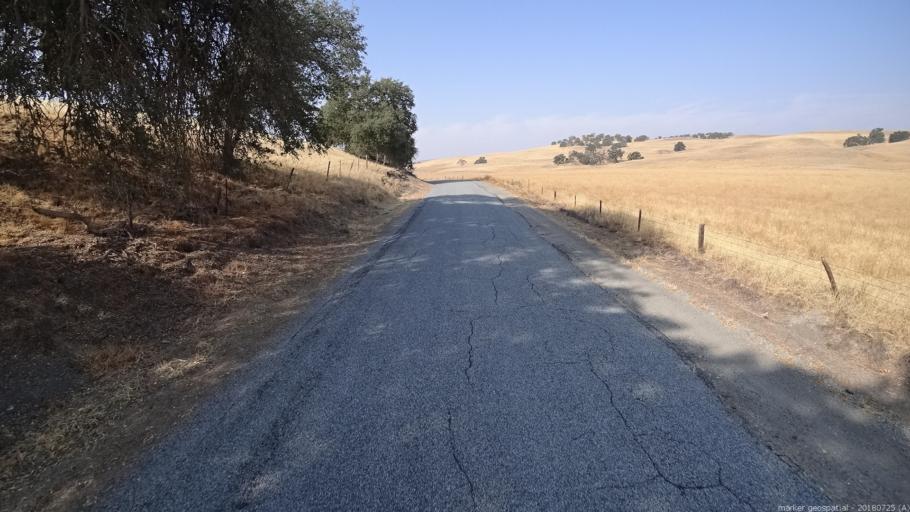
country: US
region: California
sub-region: San Luis Obispo County
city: San Miguel
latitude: 35.8020
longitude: -120.5353
